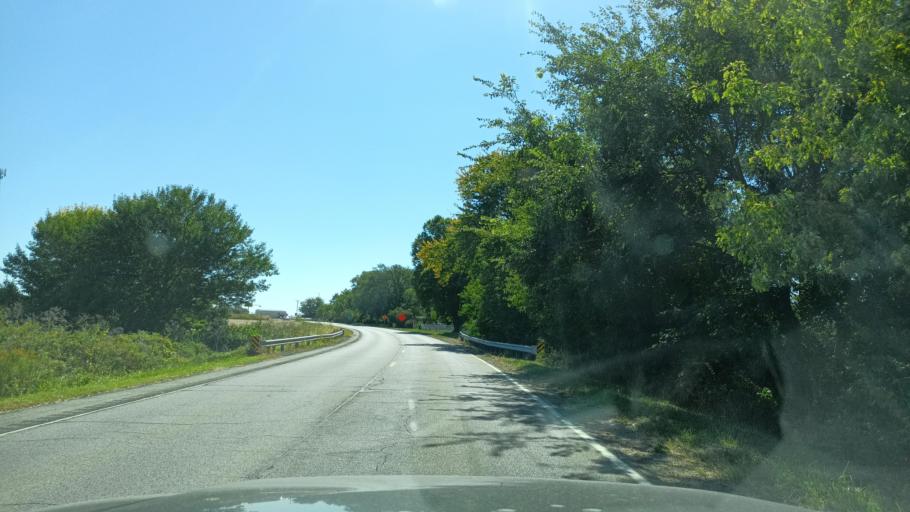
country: US
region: Illinois
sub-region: Peoria County
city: Elmwood
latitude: 40.8330
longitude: -89.8735
